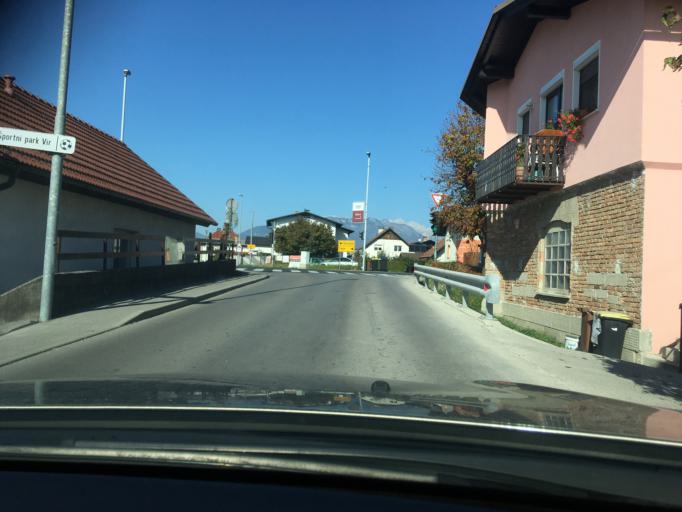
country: SI
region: Domzale
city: Vir
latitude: 46.1473
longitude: 14.6076
